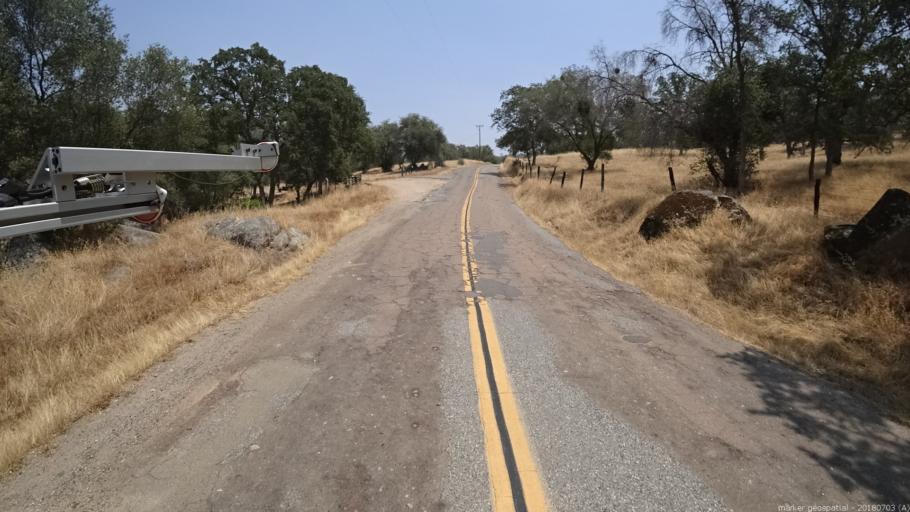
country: US
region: California
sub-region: Madera County
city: Yosemite Lakes
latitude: 37.0608
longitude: -119.6835
